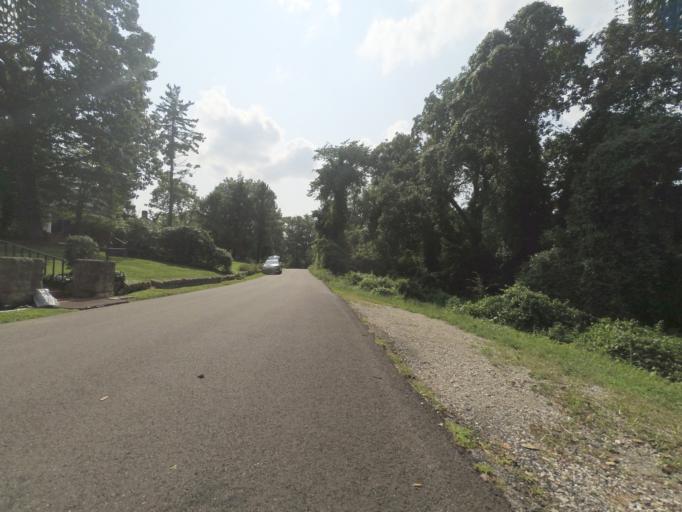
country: US
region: West Virginia
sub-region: Cabell County
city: Huntington
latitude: 38.3976
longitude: -82.4047
